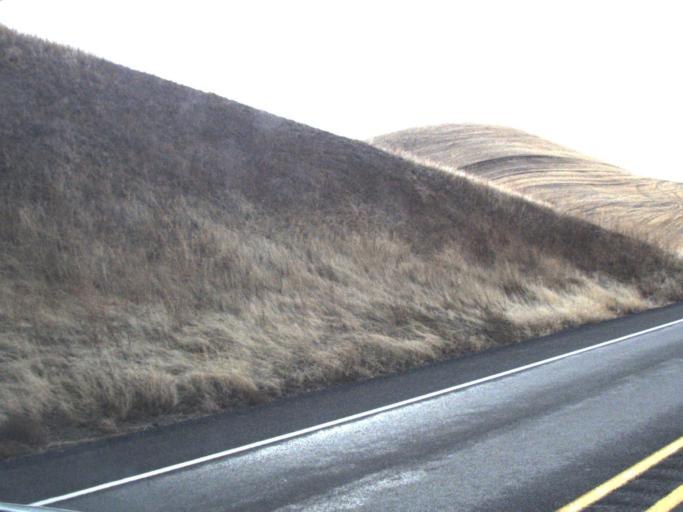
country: US
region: Washington
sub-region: Whitman County
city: Colfax
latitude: 46.8611
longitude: -117.4513
